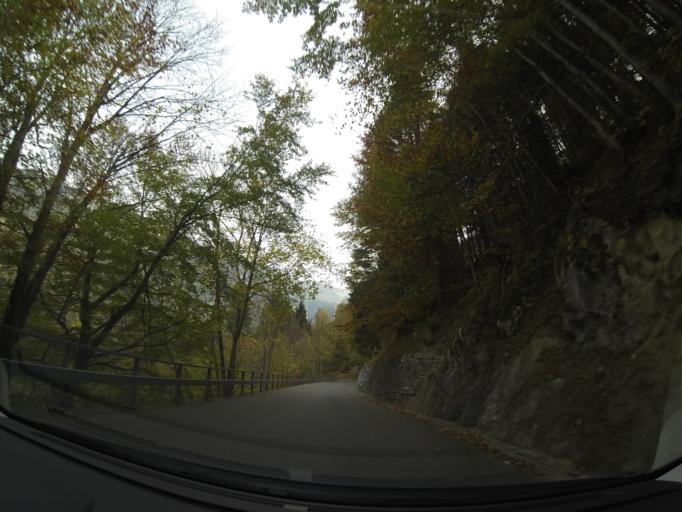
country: CH
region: Saint Gallen
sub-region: Wahlkreis Sarganserland
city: Bad Ragaz
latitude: 46.9556
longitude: 9.4746
